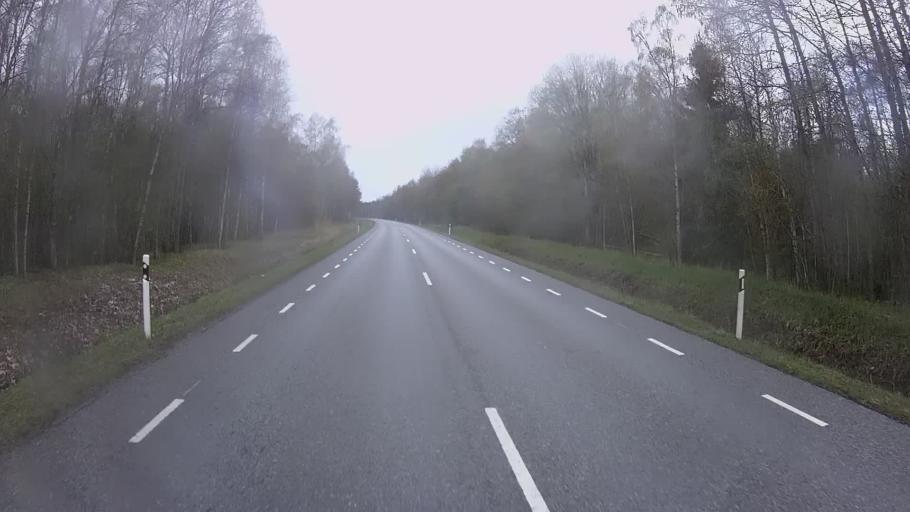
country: EE
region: Hiiumaa
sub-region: Kaerdla linn
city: Kardla
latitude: 59.0041
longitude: 22.5653
